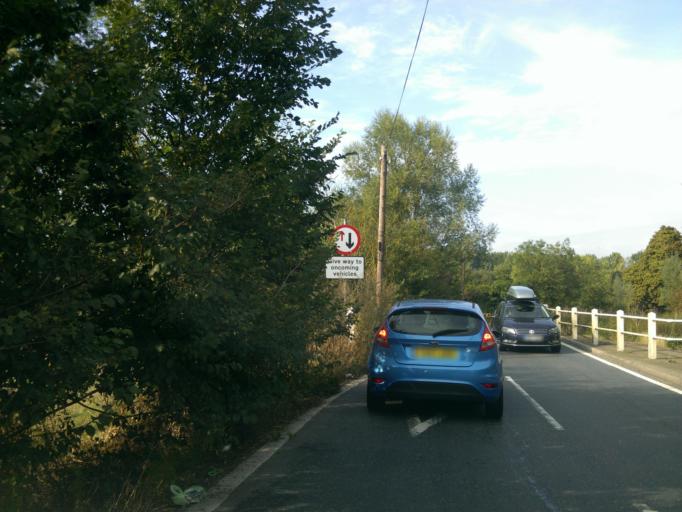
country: GB
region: England
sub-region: Essex
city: Witham
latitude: 51.8101
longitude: 0.6735
